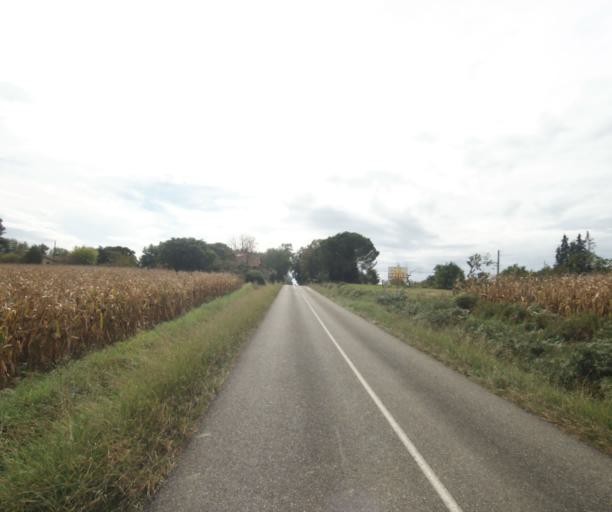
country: FR
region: Midi-Pyrenees
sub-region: Departement du Gers
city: Cazaubon
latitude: 43.8796
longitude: -0.0992
